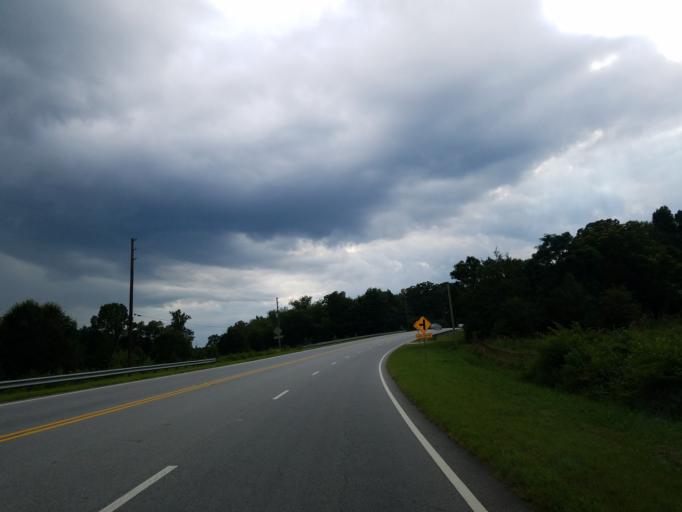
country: US
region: Georgia
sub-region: Floyd County
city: Shannon
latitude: 34.3672
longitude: -85.0744
